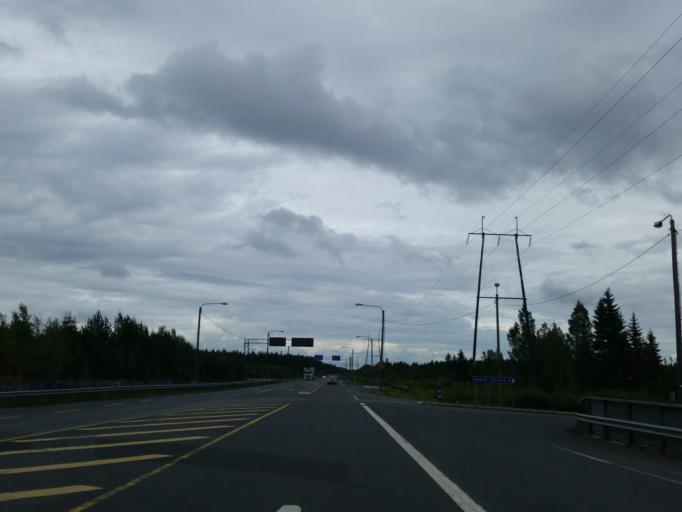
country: FI
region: Northern Savo
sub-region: Kuopio
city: Kuopio
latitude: 62.9830
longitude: 27.7319
